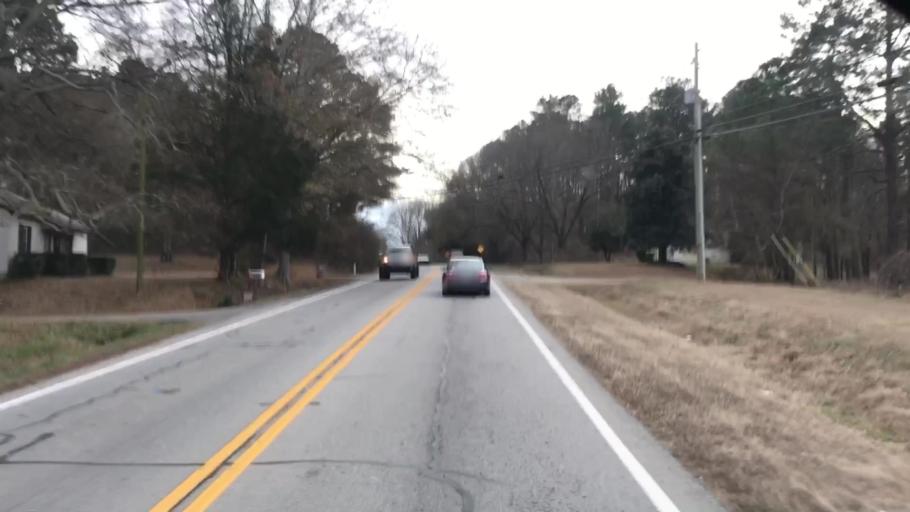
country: US
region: Georgia
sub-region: Barrow County
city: Auburn
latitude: 34.0315
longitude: -83.7741
